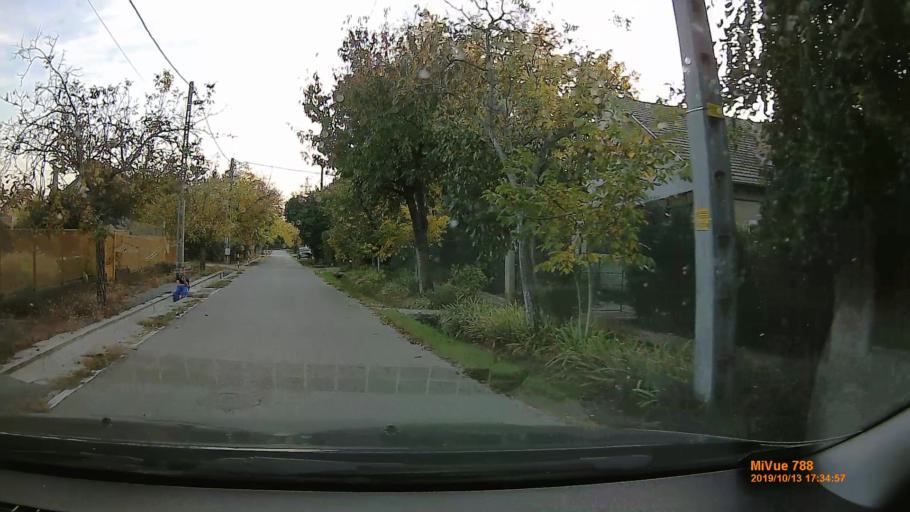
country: HU
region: Budapest
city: Budapest XVII. keruelet
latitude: 47.4949
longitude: 19.2509
